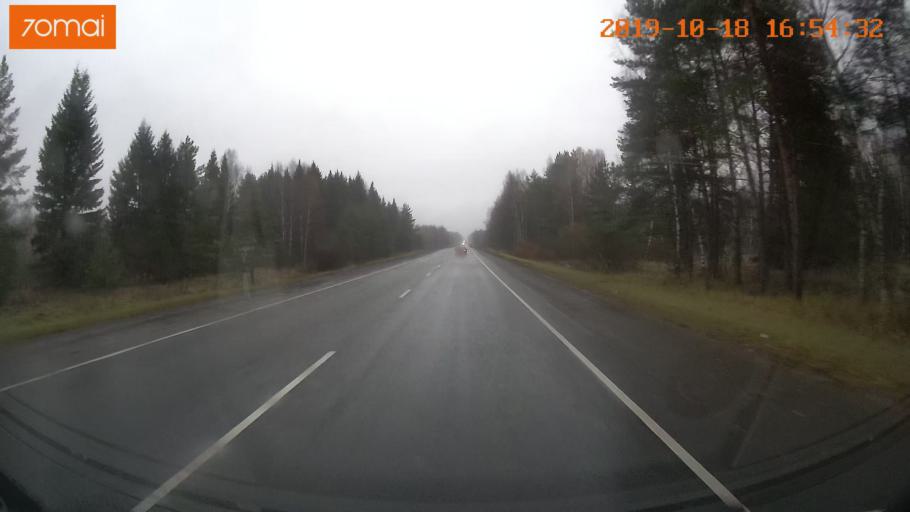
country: RU
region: Ivanovo
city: Nerl'
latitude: 56.6311
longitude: 40.5710
